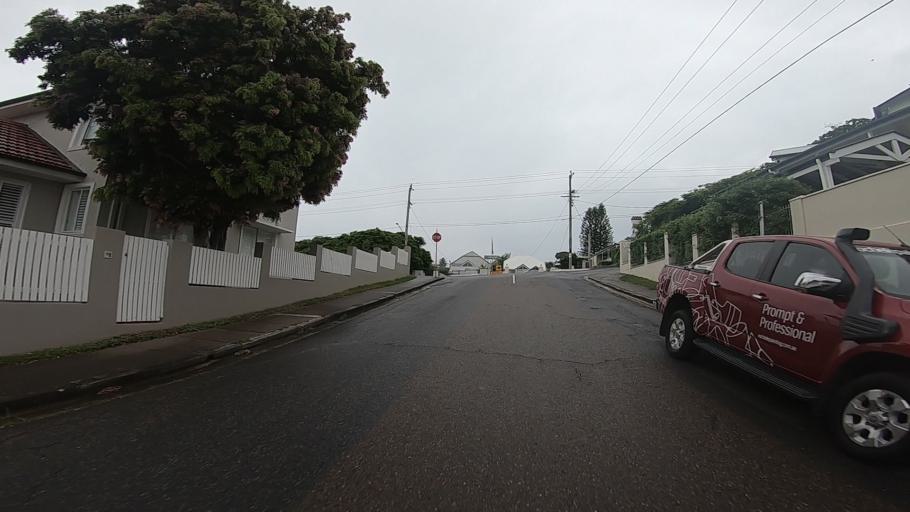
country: AU
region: Queensland
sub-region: Brisbane
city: Ascot
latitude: -27.4361
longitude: 153.0491
